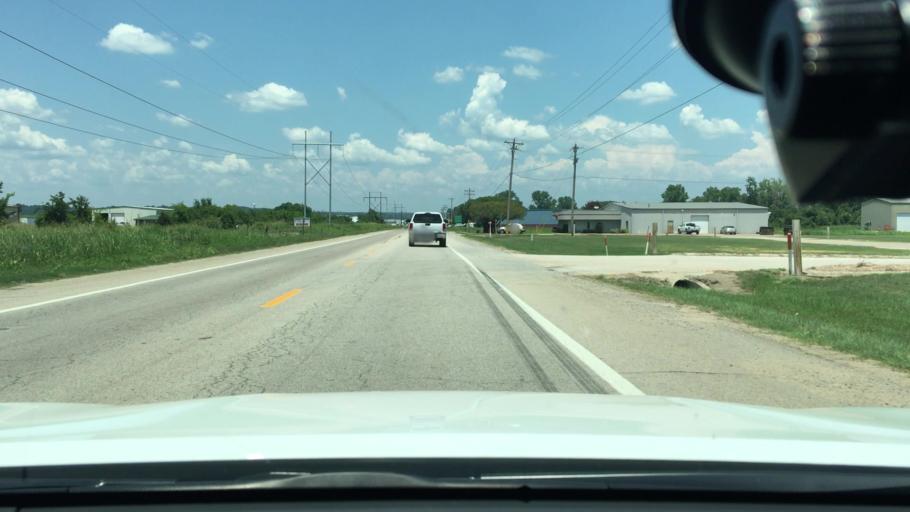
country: US
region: Arkansas
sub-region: Crawford County
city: Van Buren
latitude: 35.4063
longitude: -94.3300
